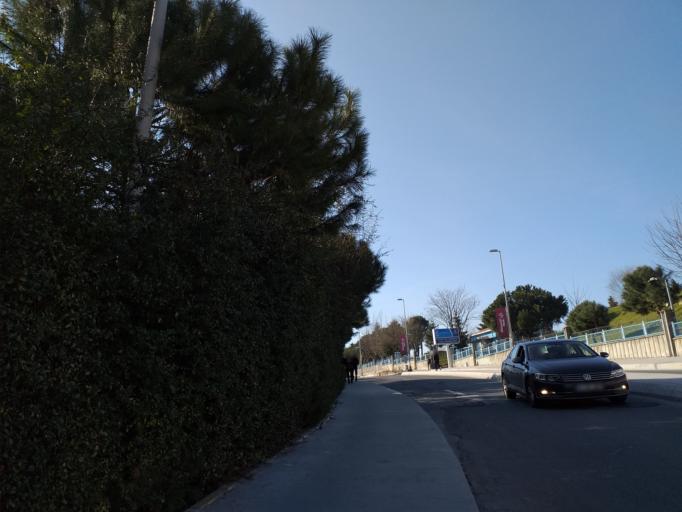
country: TR
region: Istanbul
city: Sisli
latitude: 41.1117
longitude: 29.0296
